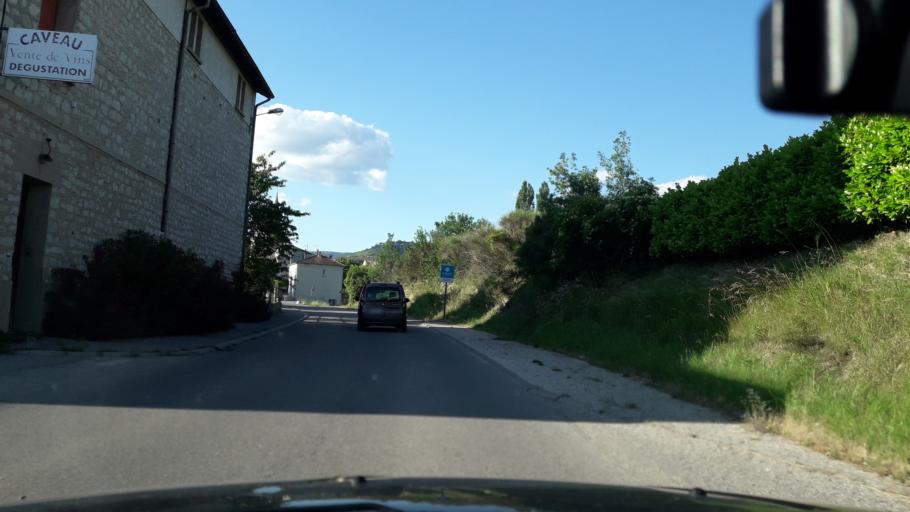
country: FR
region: Rhone-Alpes
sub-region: Departement de l'Ardeche
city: Lavilledieu
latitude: 44.6091
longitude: 4.4730
